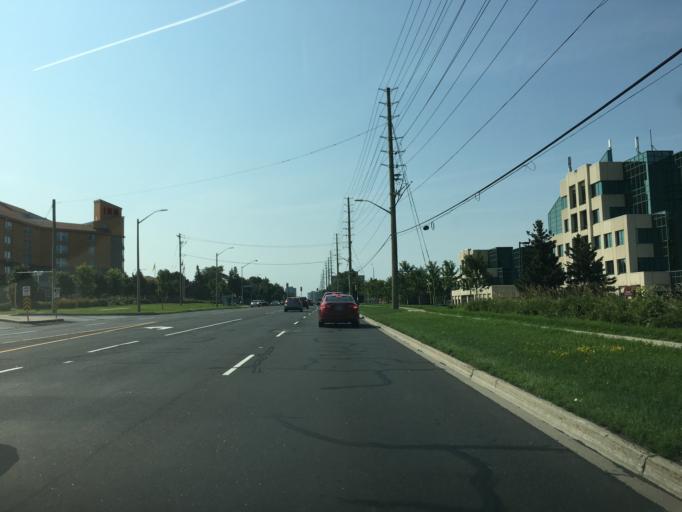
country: CA
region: Ontario
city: Markham
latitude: 43.8292
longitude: -79.3271
